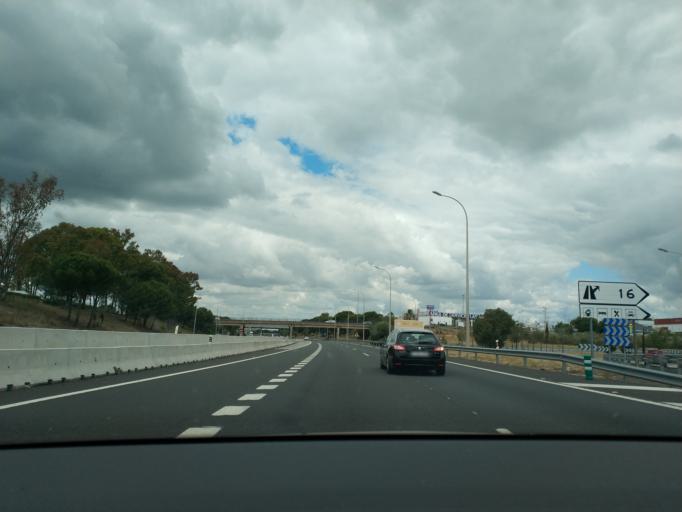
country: ES
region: Andalusia
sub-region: Provincia de Sevilla
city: Benacazon
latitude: 37.3607
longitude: -6.1979
